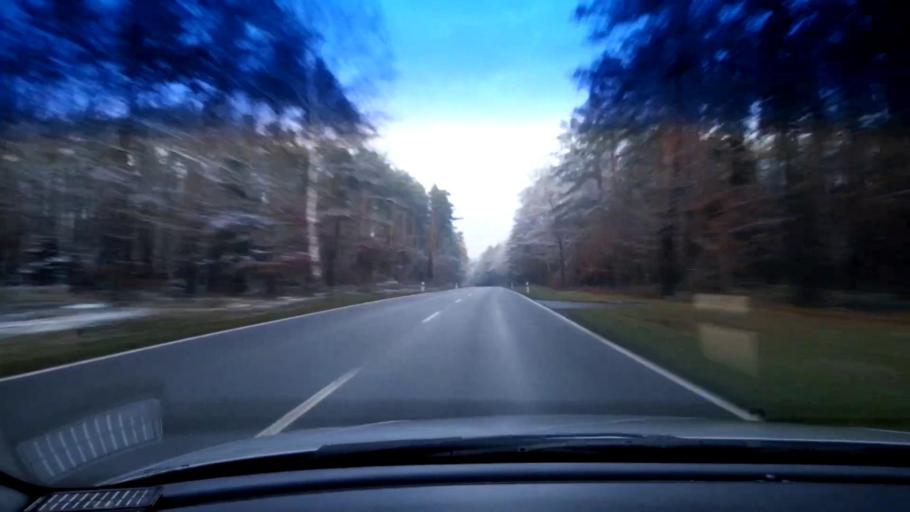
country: DE
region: Bavaria
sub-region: Upper Franconia
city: Frensdorf
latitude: 49.8046
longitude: 10.8312
